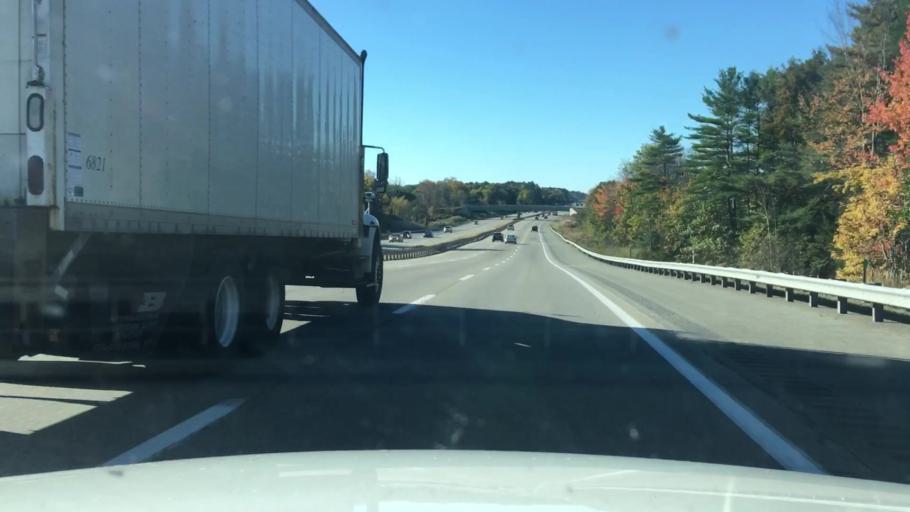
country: US
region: Maine
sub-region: Cumberland County
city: West Scarborough
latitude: 43.5950
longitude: -70.3824
